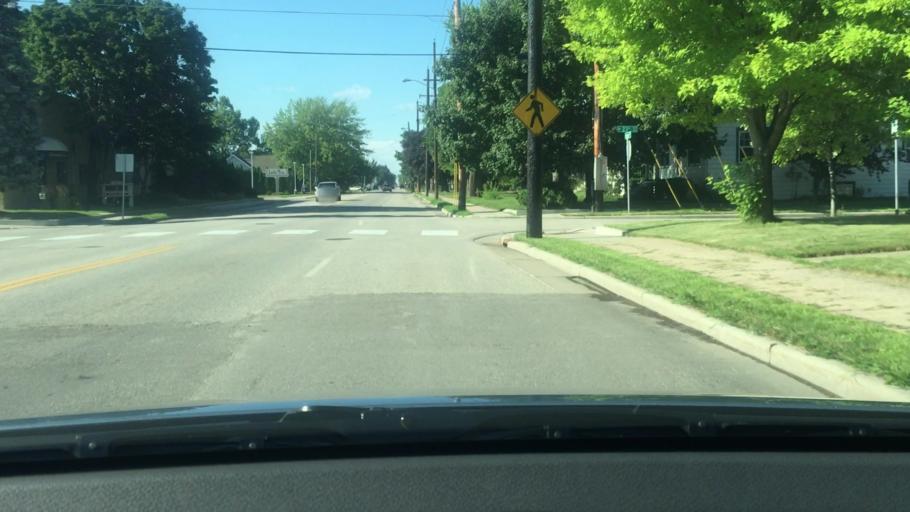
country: US
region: Wisconsin
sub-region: Winnebago County
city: Oshkosh
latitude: 43.9929
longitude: -88.5425
